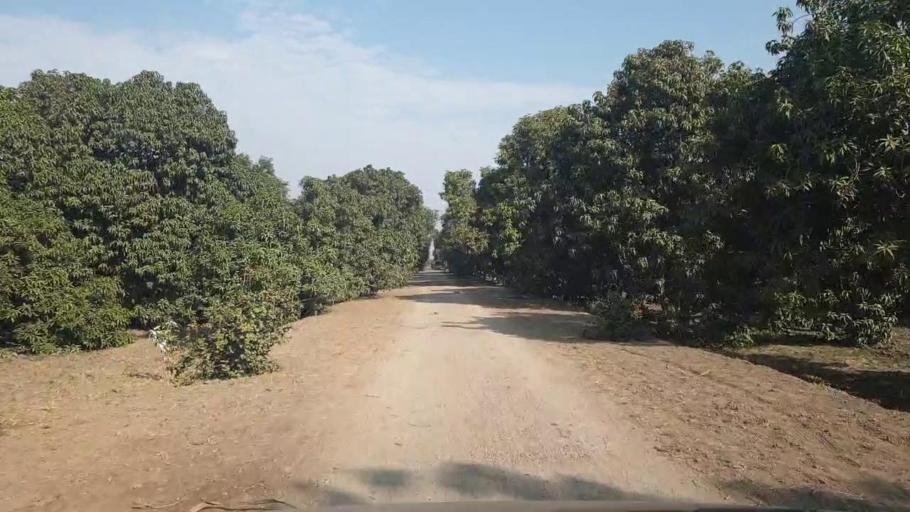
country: PK
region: Sindh
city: Tando Adam
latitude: 25.7537
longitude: 68.5882
